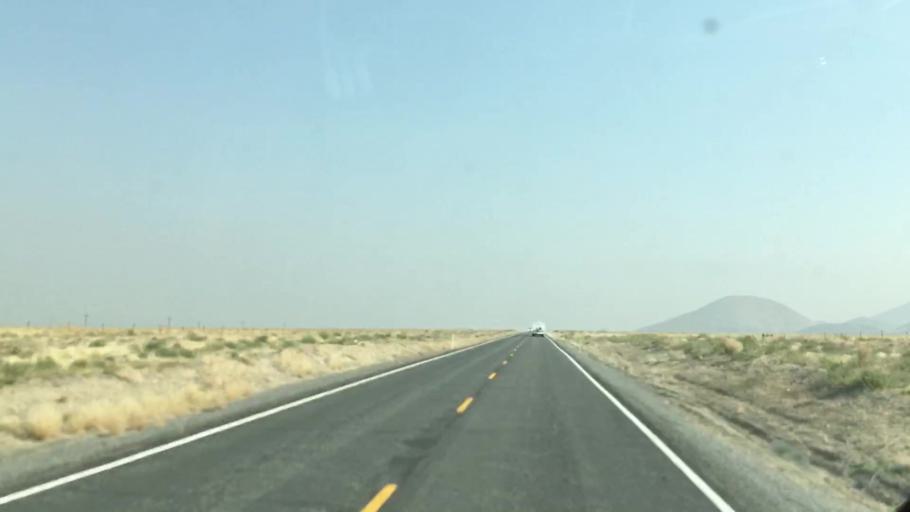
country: US
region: Nevada
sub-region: Lyon County
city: Fernley
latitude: 40.4804
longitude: -119.3345
